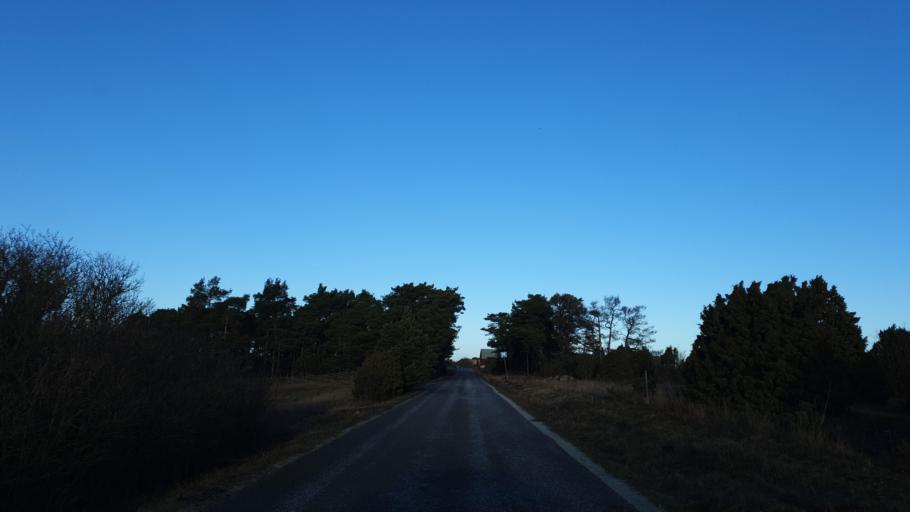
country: SE
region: Gotland
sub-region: Gotland
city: Slite
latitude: 57.3919
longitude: 18.8086
